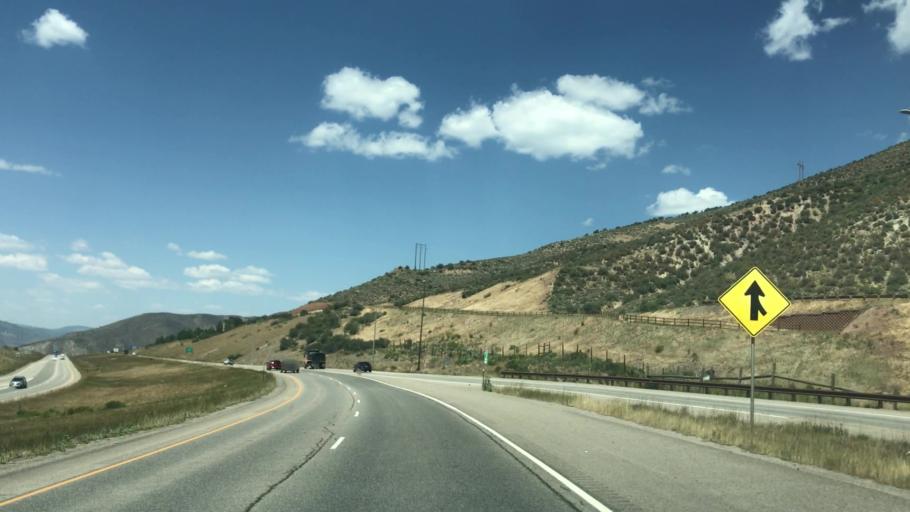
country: US
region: Colorado
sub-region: Eagle County
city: Avon
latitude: 39.6289
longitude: -106.4966
